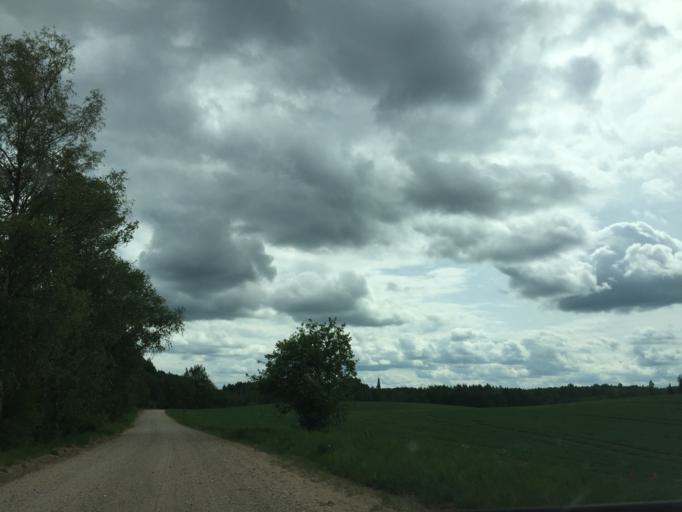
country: LV
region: Dagda
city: Dagda
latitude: 56.0566
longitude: 27.6491
